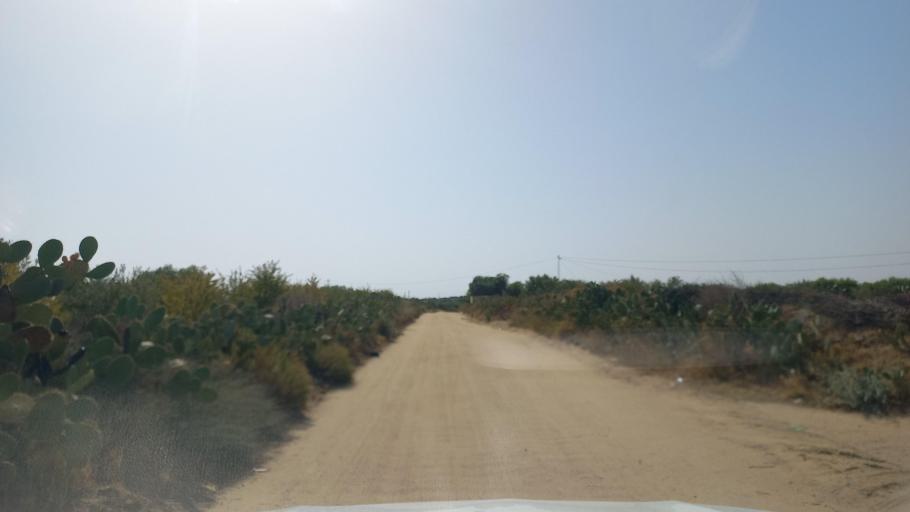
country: TN
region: Al Qasrayn
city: Kasserine
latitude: 35.2450
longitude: 9.0323
